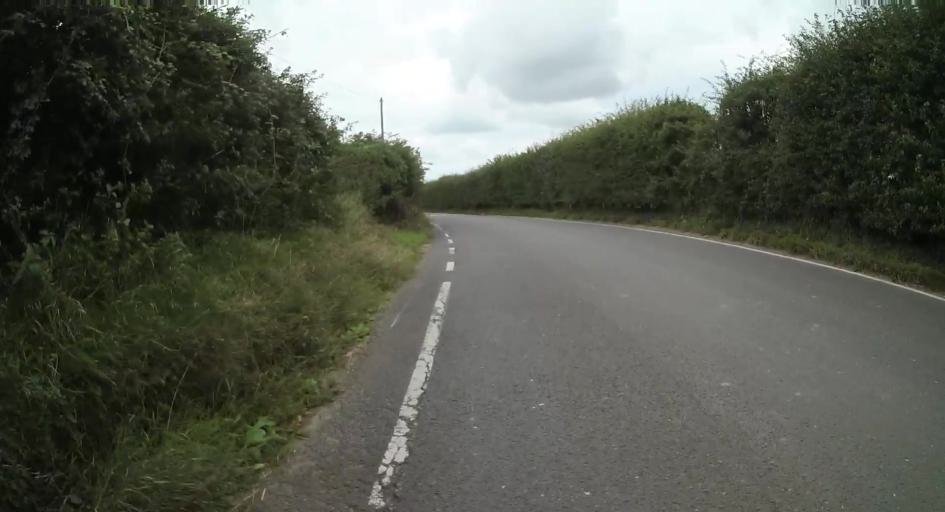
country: GB
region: England
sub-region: Isle of Wight
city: Niton
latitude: 50.6119
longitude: -1.2671
